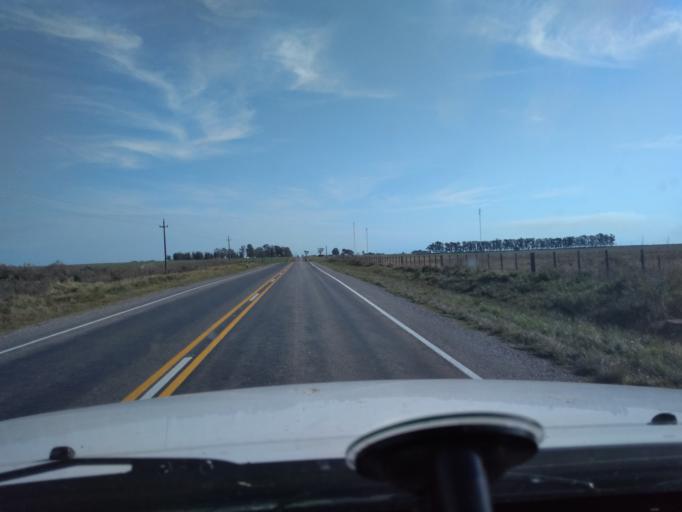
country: UY
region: Florida
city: Casupa
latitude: -34.0299
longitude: -55.8748
